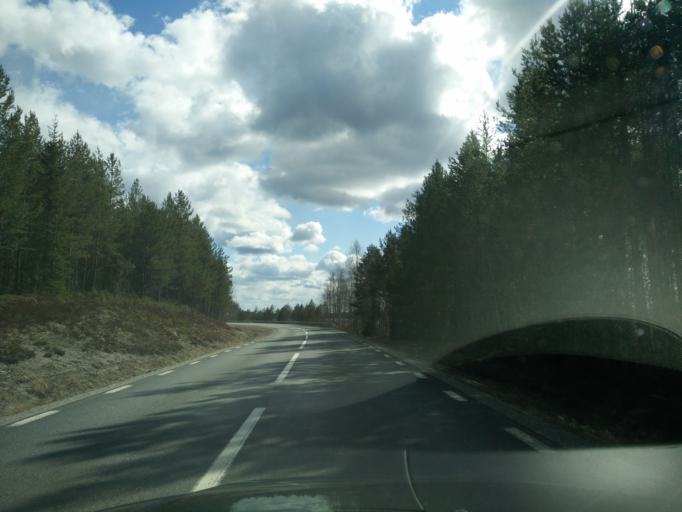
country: SE
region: Jaemtland
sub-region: Braecke Kommun
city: Braecke
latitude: 62.4552
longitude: 14.9682
